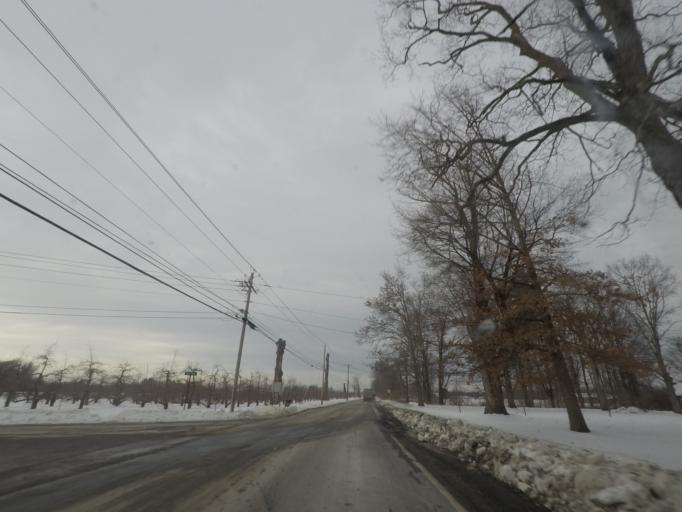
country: US
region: New York
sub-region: Columbia County
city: Kinderhook
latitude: 42.4083
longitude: -73.7044
